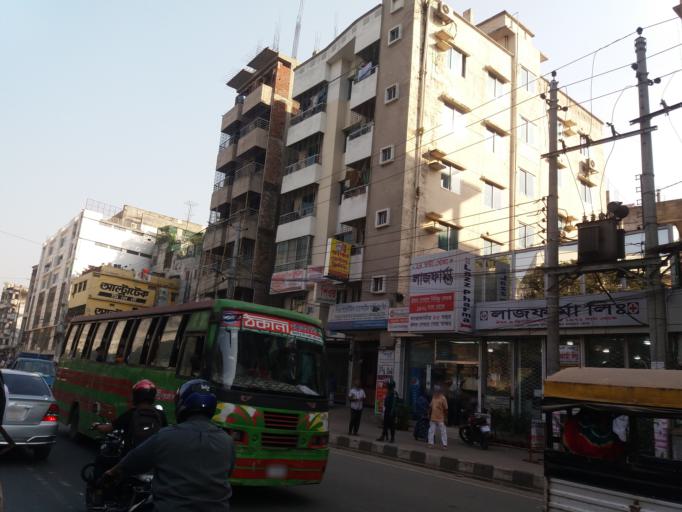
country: BD
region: Dhaka
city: Azimpur
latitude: 23.7242
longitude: 90.3982
